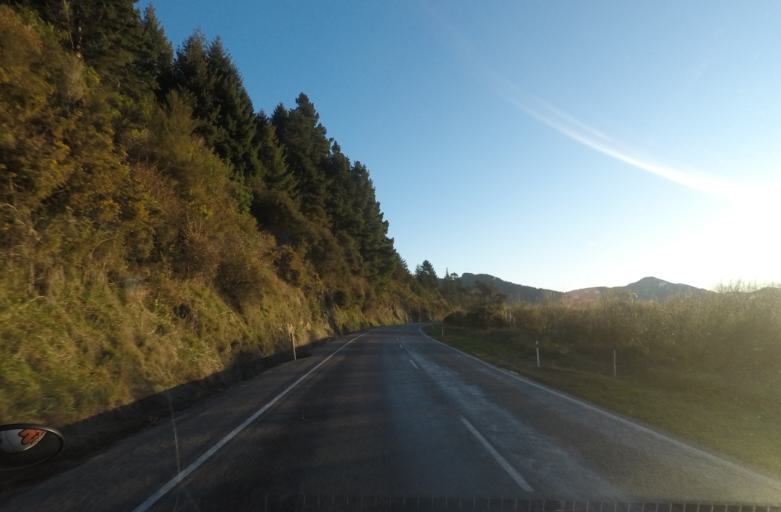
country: NZ
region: Marlborough
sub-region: Marlborough District
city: Picton
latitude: -41.2872
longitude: 173.6864
